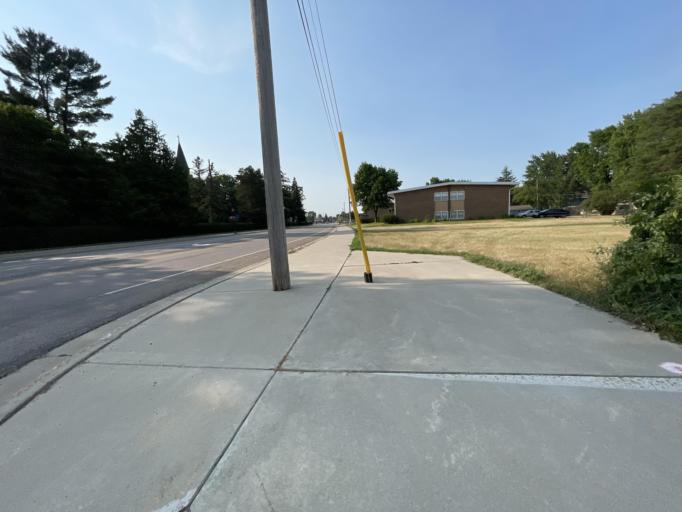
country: US
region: Minnesota
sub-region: Stearns County
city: Saint Joseph
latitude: 45.5622
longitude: -94.3168
